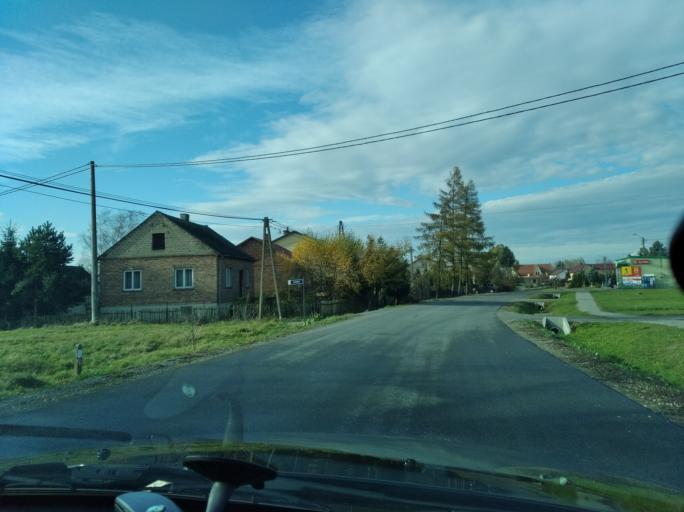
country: PL
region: Subcarpathian Voivodeship
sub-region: Powiat ropczycko-sedziszowski
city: Sedziszow Malopolski
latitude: 50.0780
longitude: 21.7412
